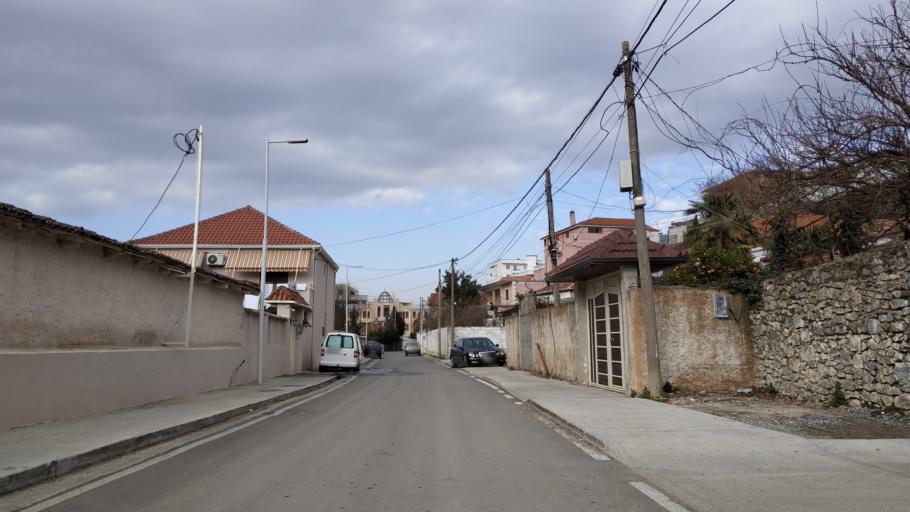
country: AL
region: Shkoder
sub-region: Rrethi i Shkodres
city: Shkoder
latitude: 42.0552
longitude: 19.5033
